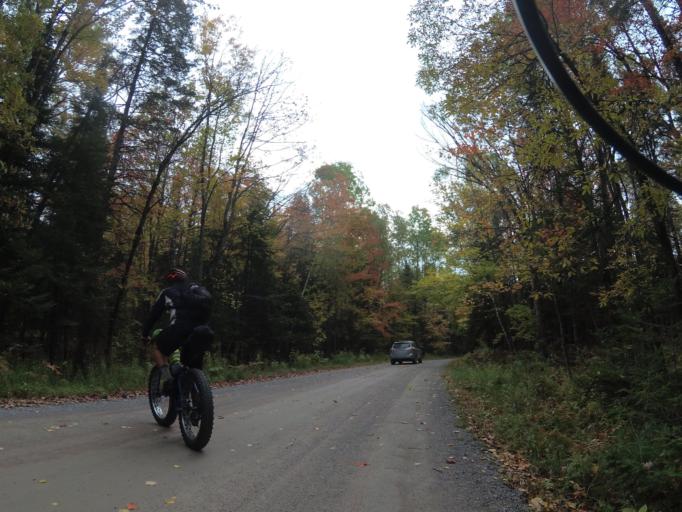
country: CA
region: Ontario
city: Renfrew
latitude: 45.2596
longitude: -77.2077
